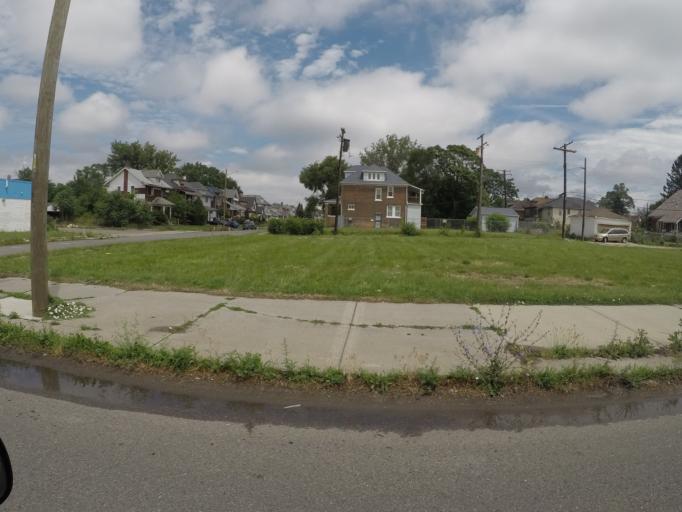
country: US
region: Michigan
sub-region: Wayne County
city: Dearborn
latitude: 42.3450
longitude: -83.1403
